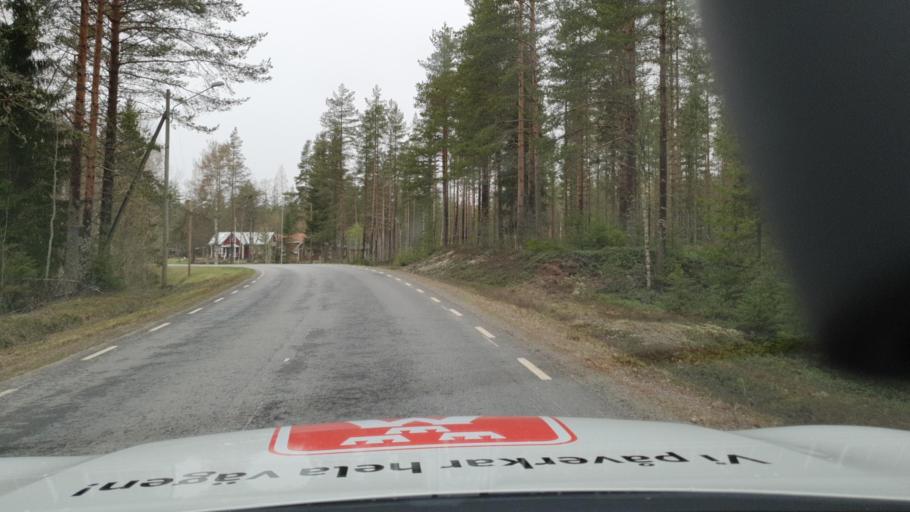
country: SE
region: Vaesterbotten
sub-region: Nordmalings Kommun
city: Nordmaling
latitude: 63.7063
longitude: 19.6026
